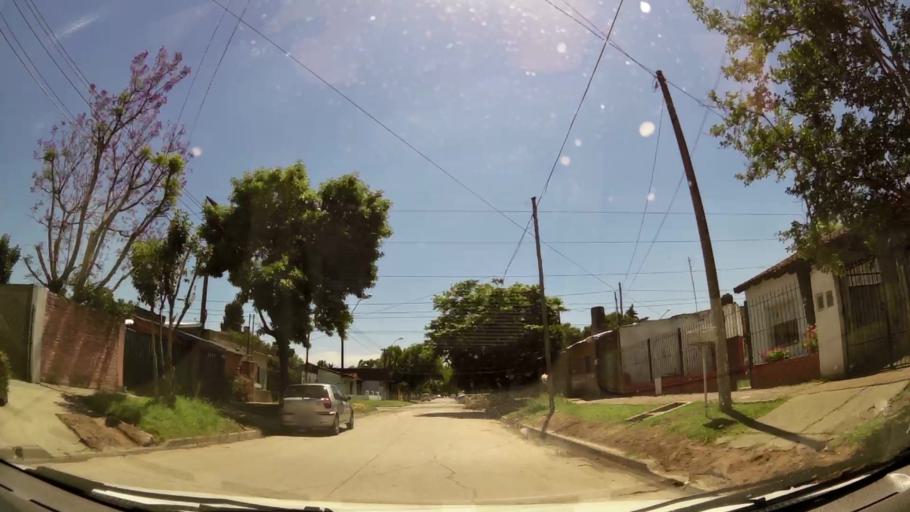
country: AR
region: Buenos Aires
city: Ituzaingo
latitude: -34.6775
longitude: -58.6741
